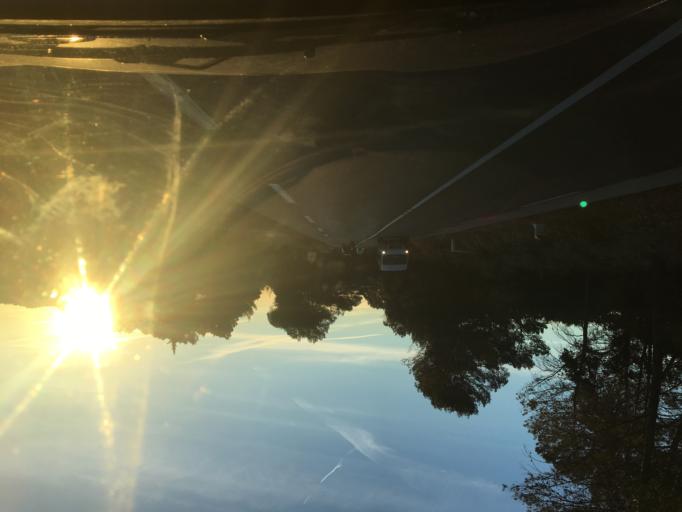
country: FR
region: Provence-Alpes-Cote d'Azur
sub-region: Departement du Var
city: Taradeau
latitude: 43.4615
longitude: 6.4046
